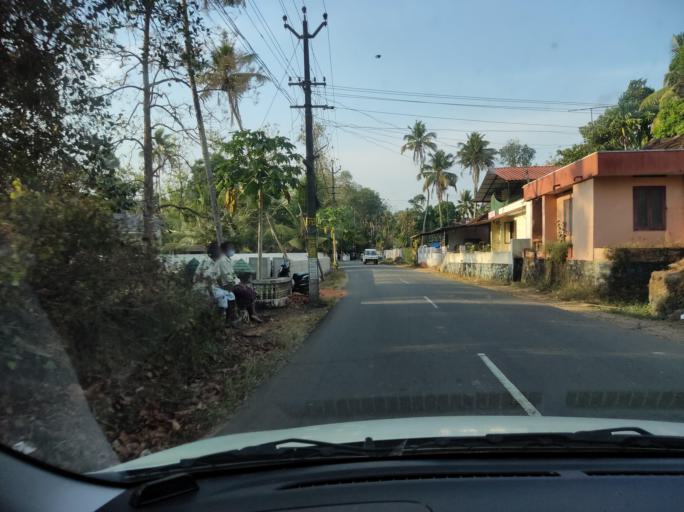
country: IN
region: Kerala
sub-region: Kottayam
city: Kottayam
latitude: 9.6747
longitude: 76.5058
